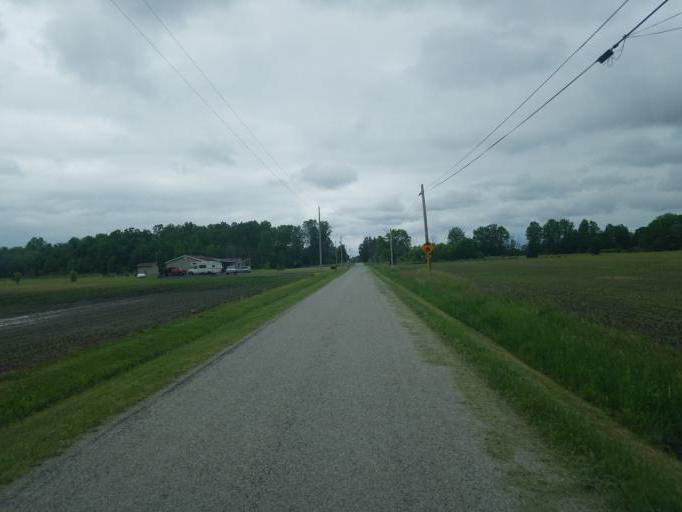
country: US
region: Ohio
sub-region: Morrow County
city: Cardington
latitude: 40.5434
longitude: -82.9601
